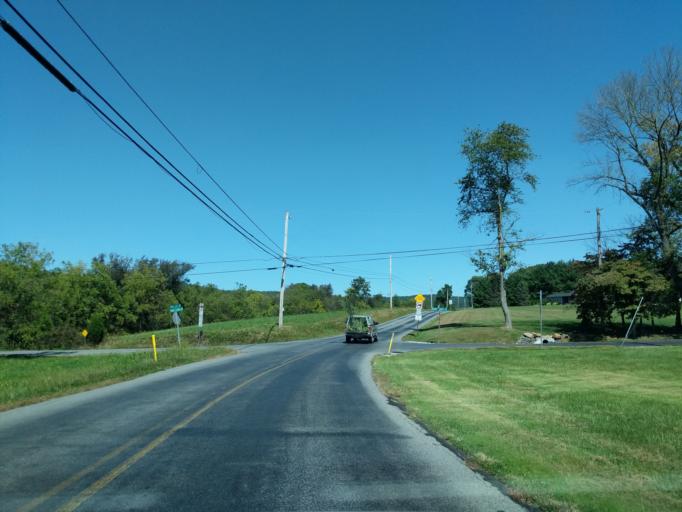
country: US
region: Pennsylvania
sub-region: Montgomery County
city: East Greenville
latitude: 40.4226
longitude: -75.5024
